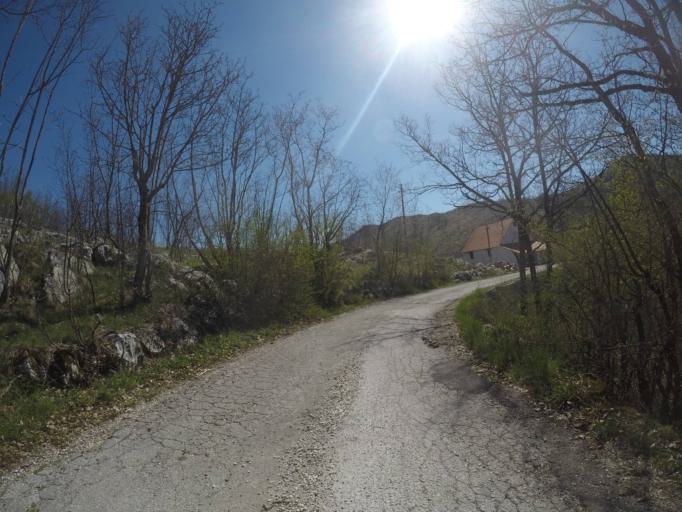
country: ME
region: Cetinje
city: Cetinje
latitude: 42.5373
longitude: 18.9841
